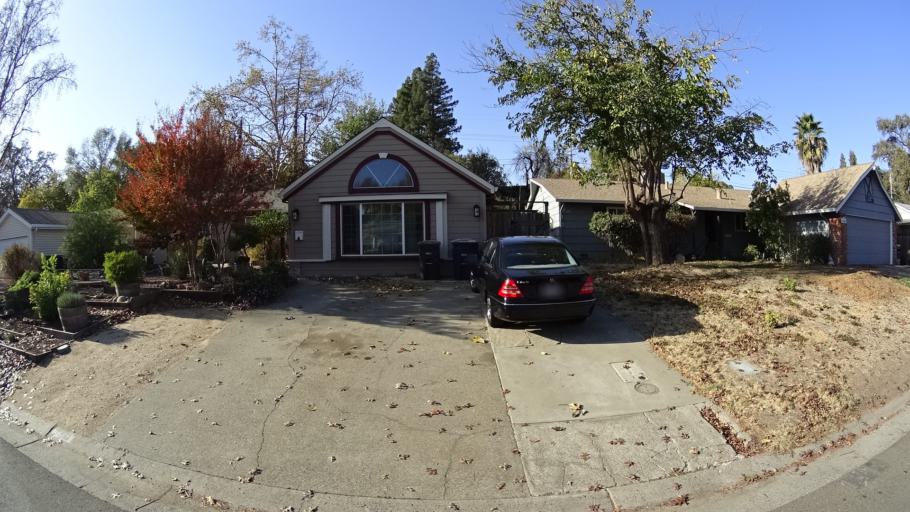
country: US
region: California
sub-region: Sacramento County
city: Fair Oaks
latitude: 38.6727
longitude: -121.2894
